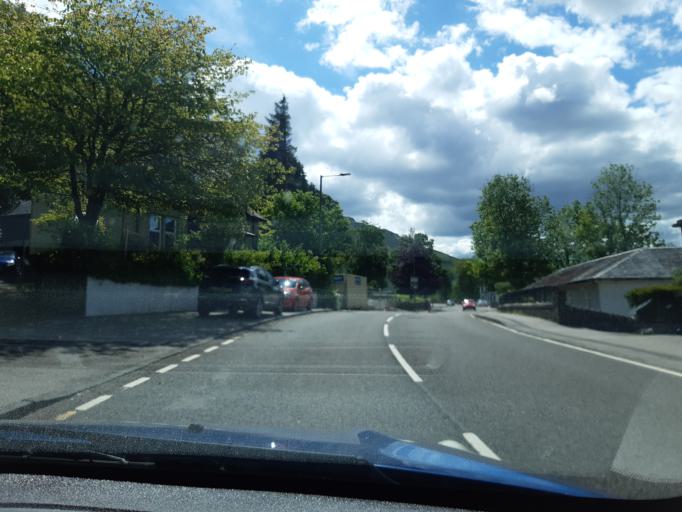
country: GB
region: Scotland
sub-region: Argyll and Bute
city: Garelochhead
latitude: 56.2033
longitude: -4.7436
